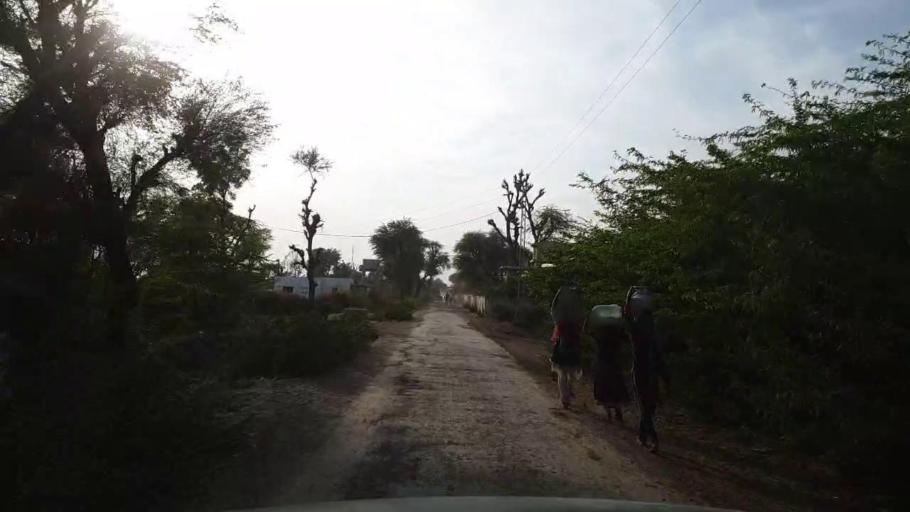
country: PK
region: Sindh
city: Kunri
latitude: 25.1951
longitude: 69.5209
